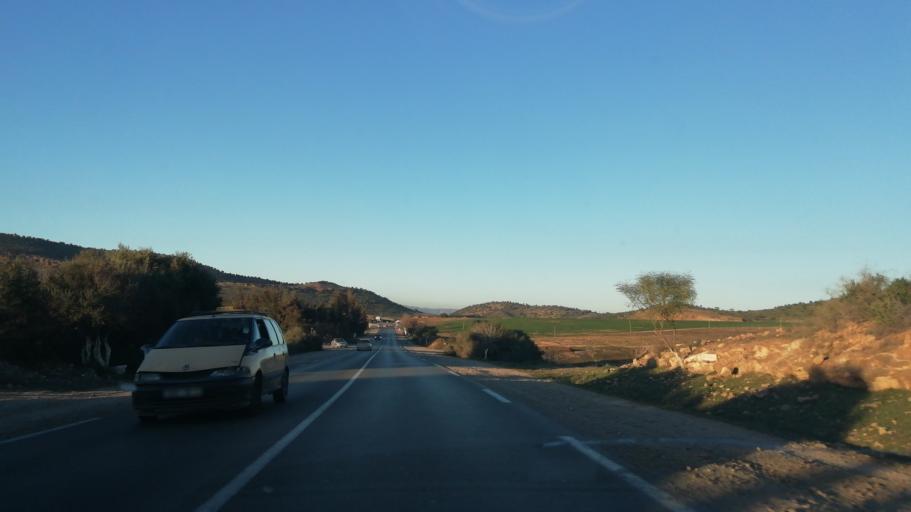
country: DZ
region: Tlemcen
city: Nedroma
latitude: 34.8580
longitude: -1.6789
